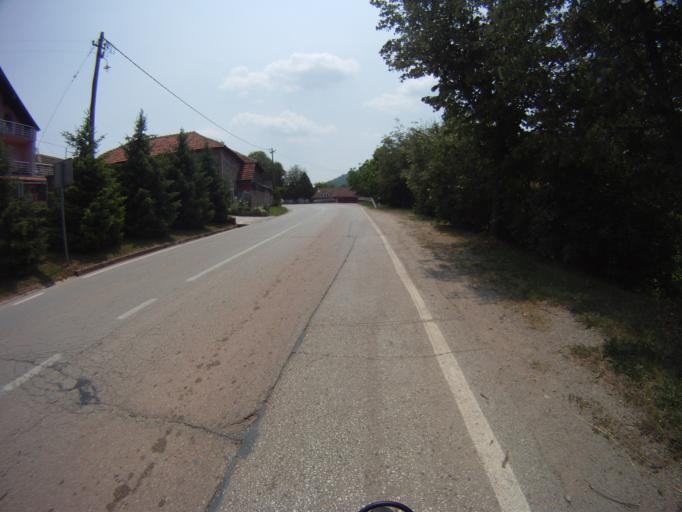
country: RS
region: Central Serbia
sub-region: Nisavski Okrug
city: Gadzin Han
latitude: 43.2406
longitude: 22.0152
